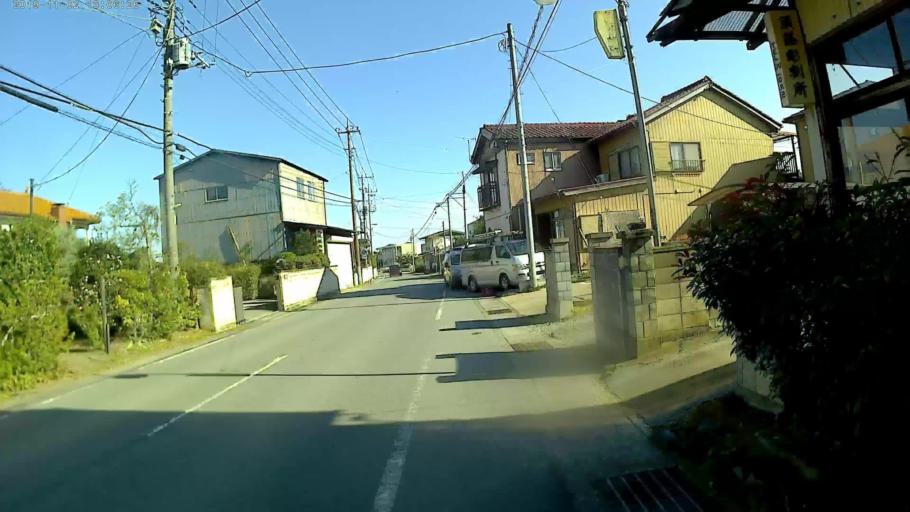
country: JP
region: Gunma
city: Annaka
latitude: 36.3365
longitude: 138.9367
